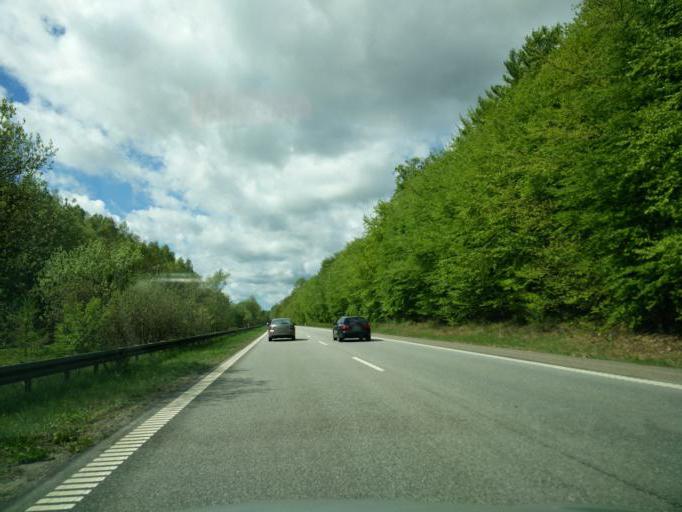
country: DK
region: Capital Region
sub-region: Fureso Kommune
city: Farum
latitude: 55.8344
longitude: 12.3635
